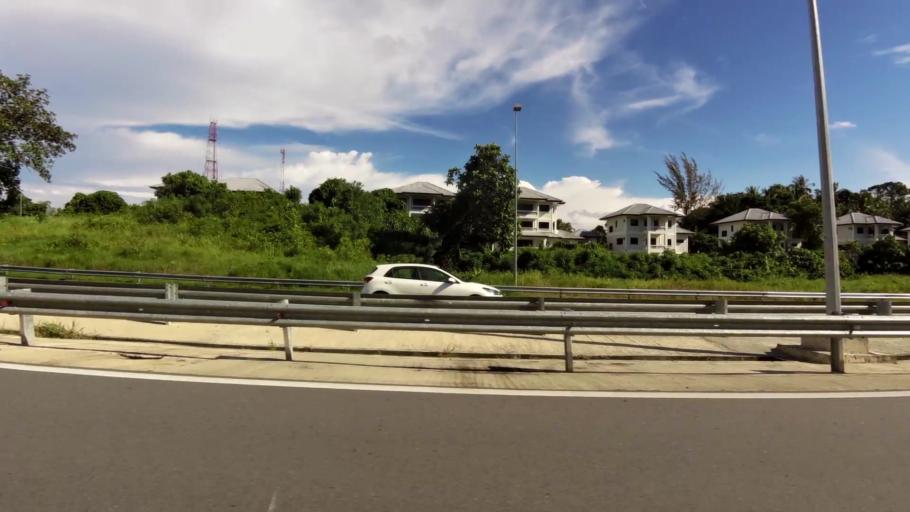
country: BN
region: Brunei and Muara
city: Bandar Seri Begawan
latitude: 4.9865
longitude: 114.9535
